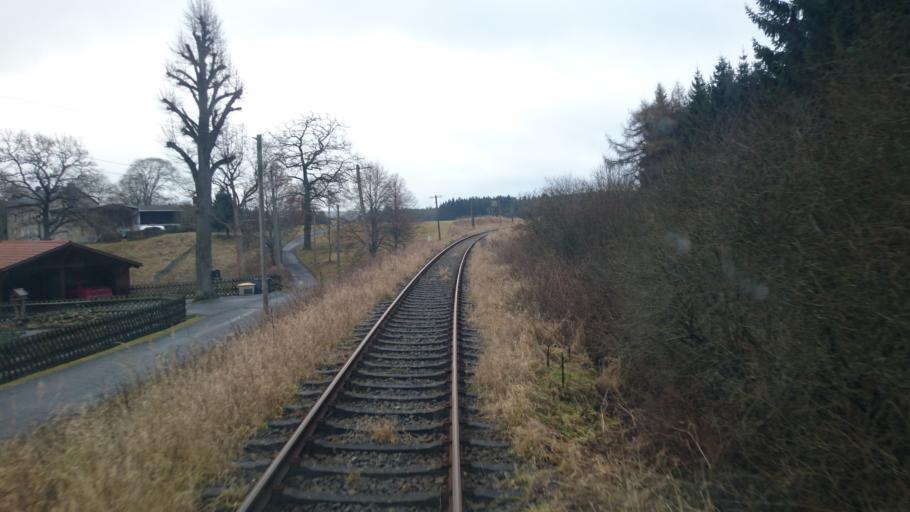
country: DE
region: Saxony
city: Muhltroff
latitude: 50.5602
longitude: 11.8996
